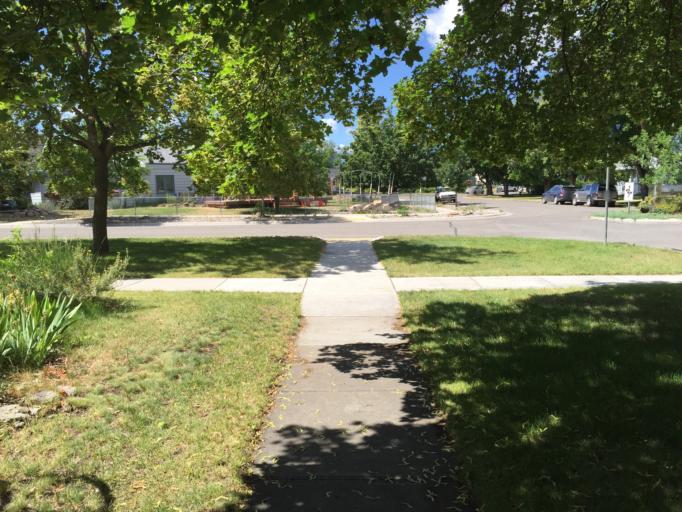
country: US
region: Montana
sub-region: Missoula County
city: Missoula
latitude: 46.8566
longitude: -113.9999
